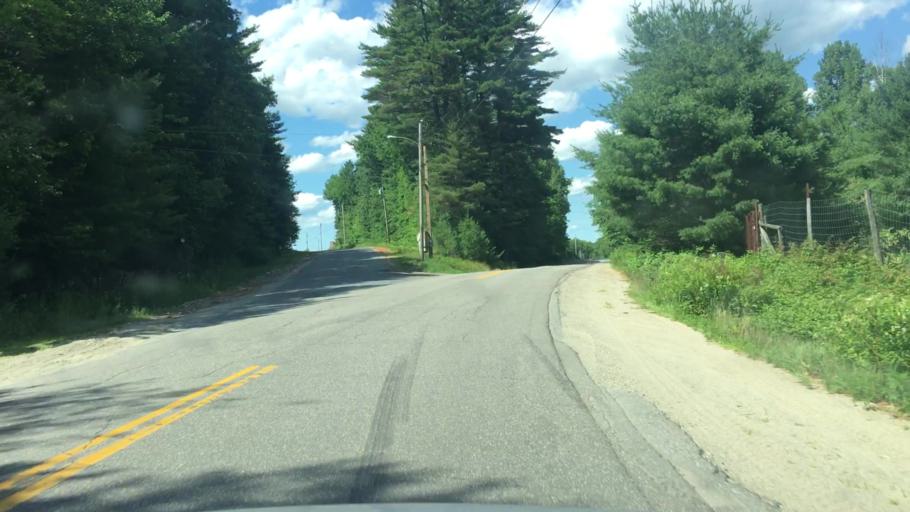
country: US
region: Maine
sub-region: Franklin County
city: Chesterville
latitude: 44.5804
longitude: -70.0904
